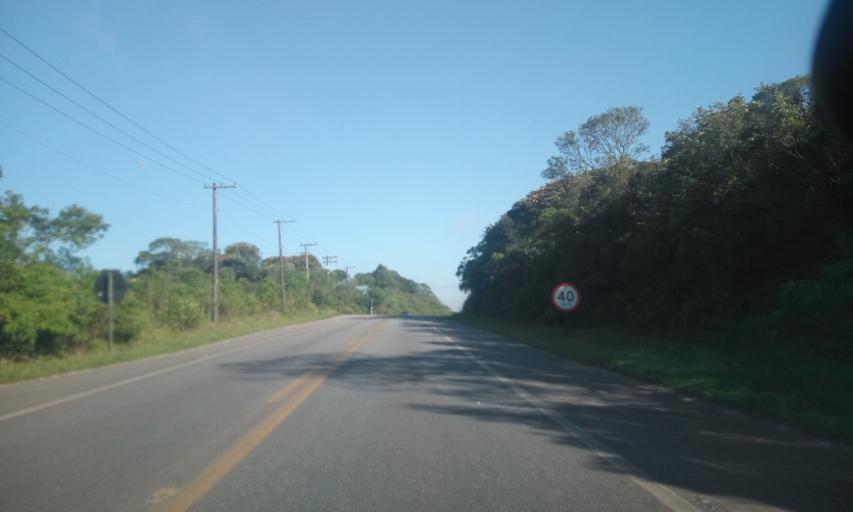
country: BR
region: Sao Paulo
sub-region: Cubatao
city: Cubatao
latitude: -23.8320
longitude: -46.4729
